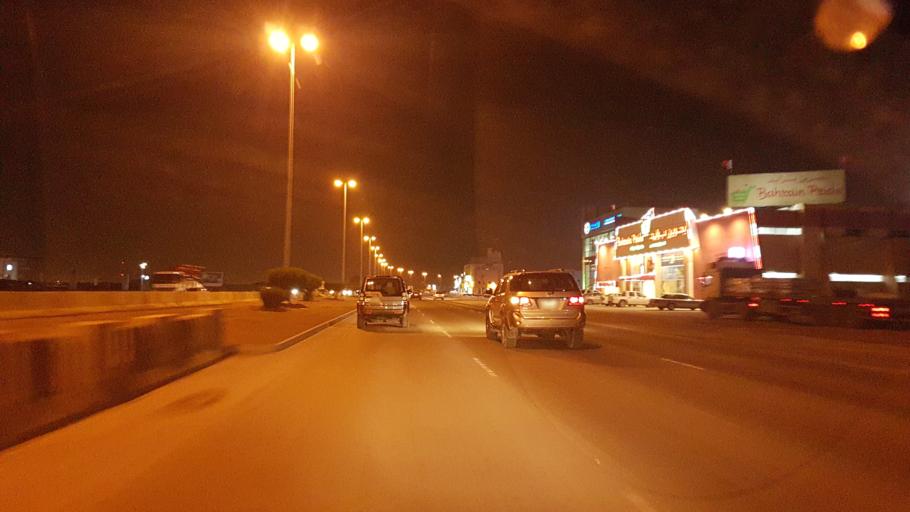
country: BH
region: Northern
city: Sitrah
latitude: 26.1549
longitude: 50.6116
